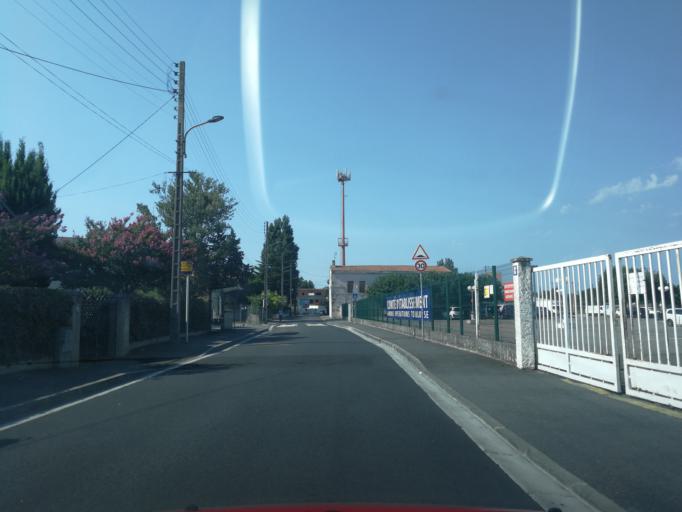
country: FR
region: Midi-Pyrenees
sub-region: Departement de la Haute-Garonne
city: Blagnac
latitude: 43.6217
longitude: 1.4082
